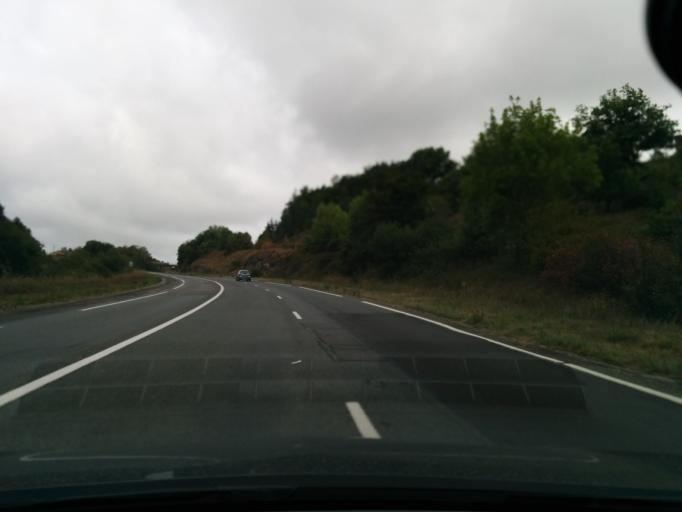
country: FR
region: Midi-Pyrenees
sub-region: Departement du Lot
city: Cahors
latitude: 44.4328
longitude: 1.4267
